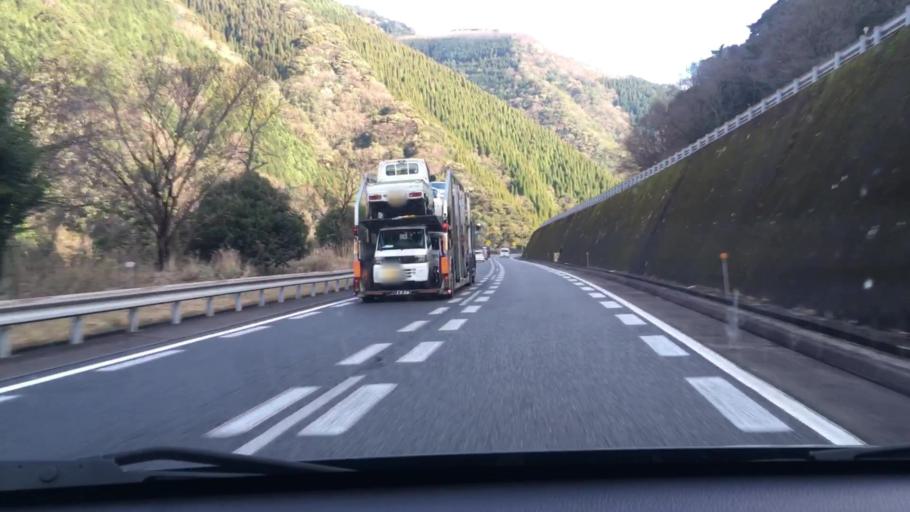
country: JP
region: Kumamoto
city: Hitoyoshi
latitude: 32.3275
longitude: 130.7524
